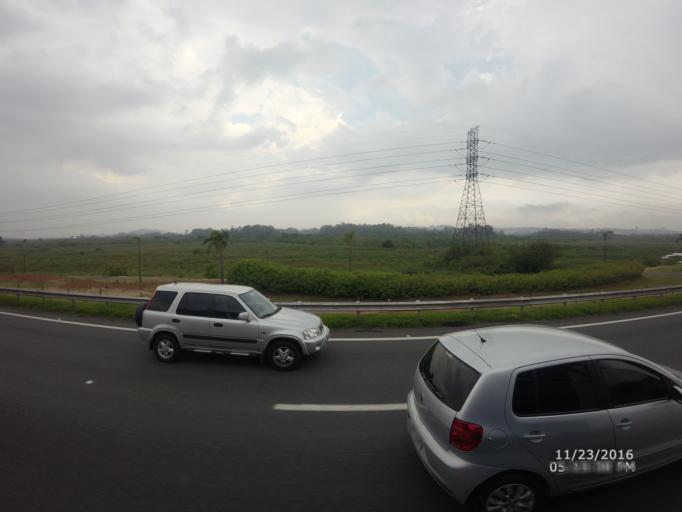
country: BR
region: Sao Paulo
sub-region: Guarulhos
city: Guarulhos
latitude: -23.4823
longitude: -46.5255
